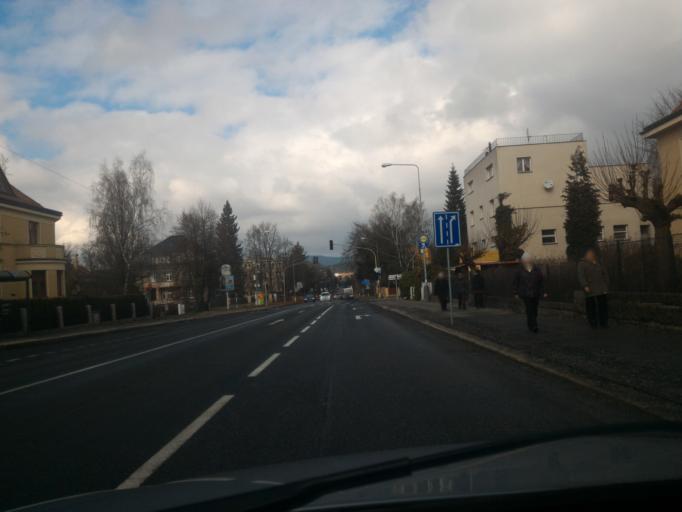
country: CZ
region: Liberecky
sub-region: Okres Jablonec nad Nisou
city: Jablonec nad Nisou
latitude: 50.7308
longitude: 15.1698
